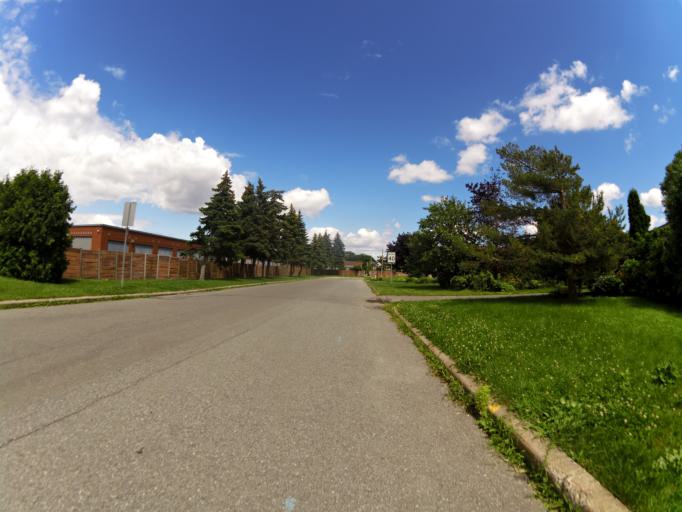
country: CA
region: Ontario
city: Ottawa
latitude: 45.3699
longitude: -75.7180
